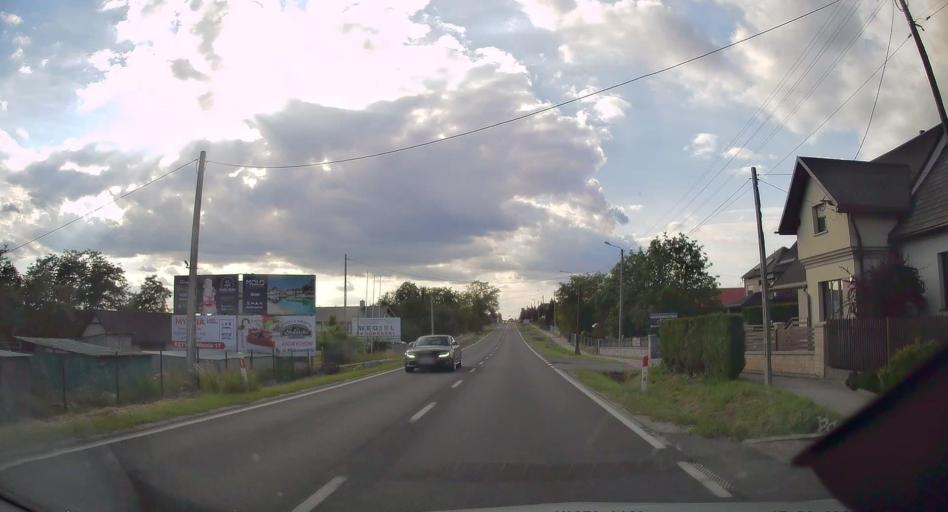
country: PL
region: Lesser Poland Voivodeship
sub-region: Powiat wadowicki
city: Roczyny
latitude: 49.8673
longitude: 19.3087
